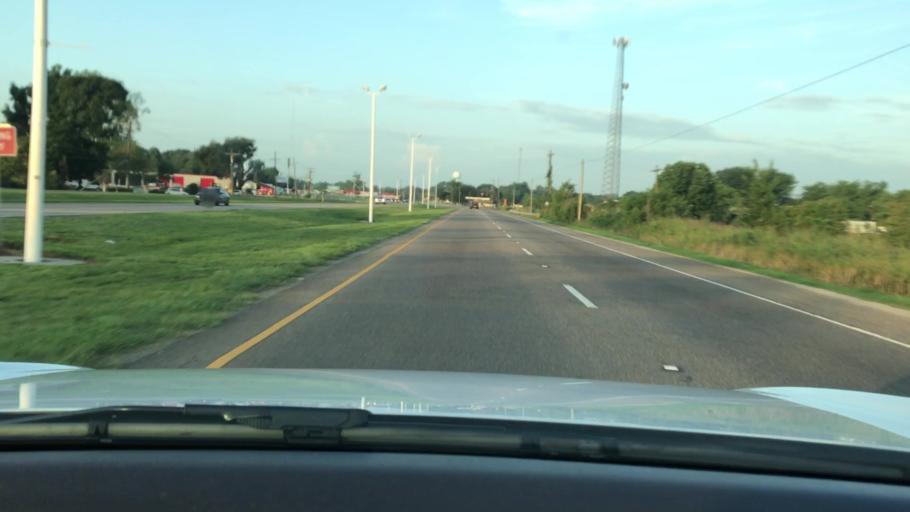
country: US
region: Louisiana
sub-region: West Baton Rouge Parish
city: Addis
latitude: 30.3685
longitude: -91.2584
